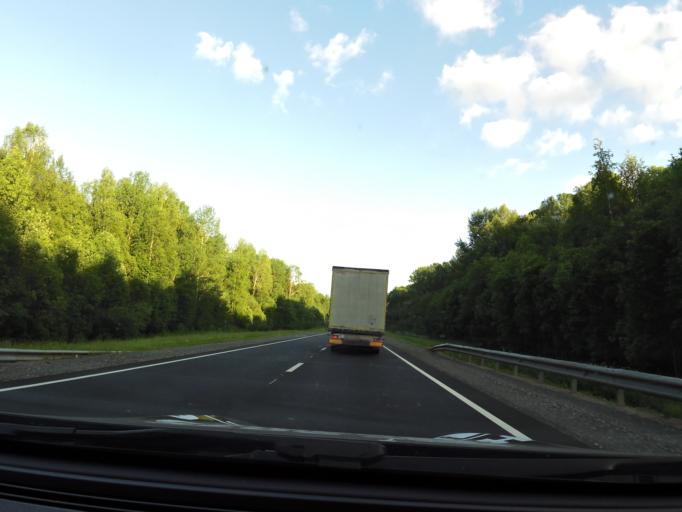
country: RU
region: Vologda
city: Gryazovets
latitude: 58.9567
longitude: 40.1654
